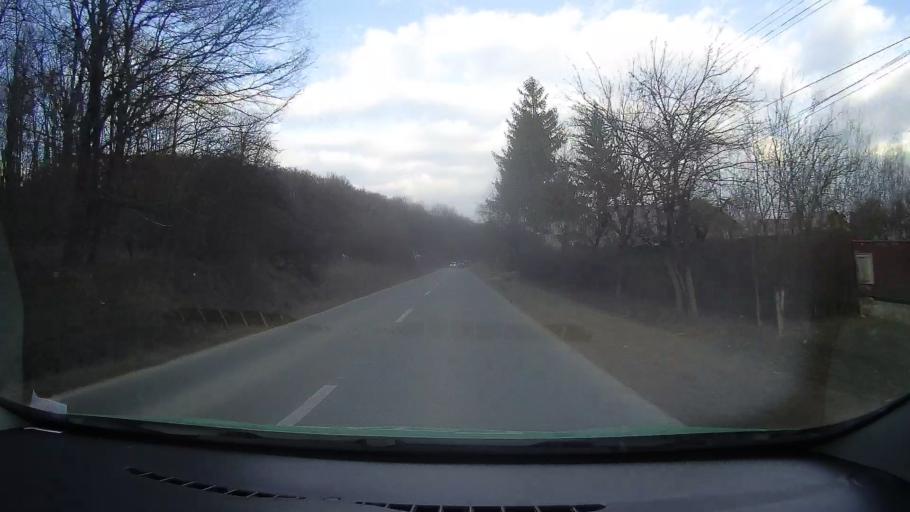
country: RO
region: Dambovita
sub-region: Comuna Gura Ocnitei
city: Gura Ocnitei
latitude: 44.9442
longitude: 25.5845
